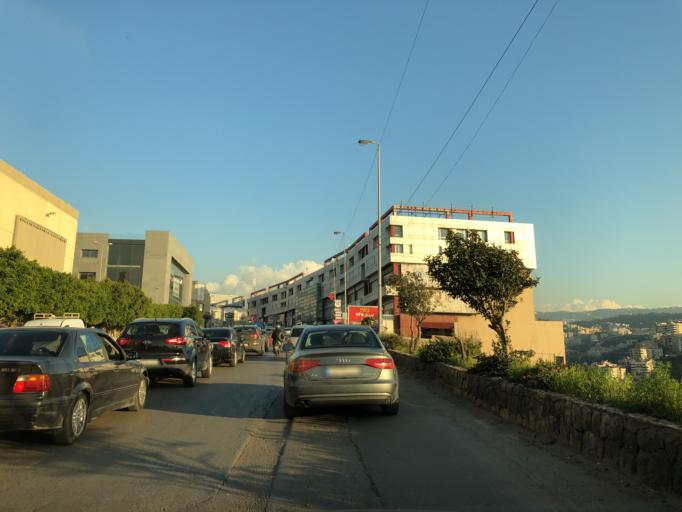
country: LB
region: Mont-Liban
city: Baabda
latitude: 33.8609
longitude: 35.5512
